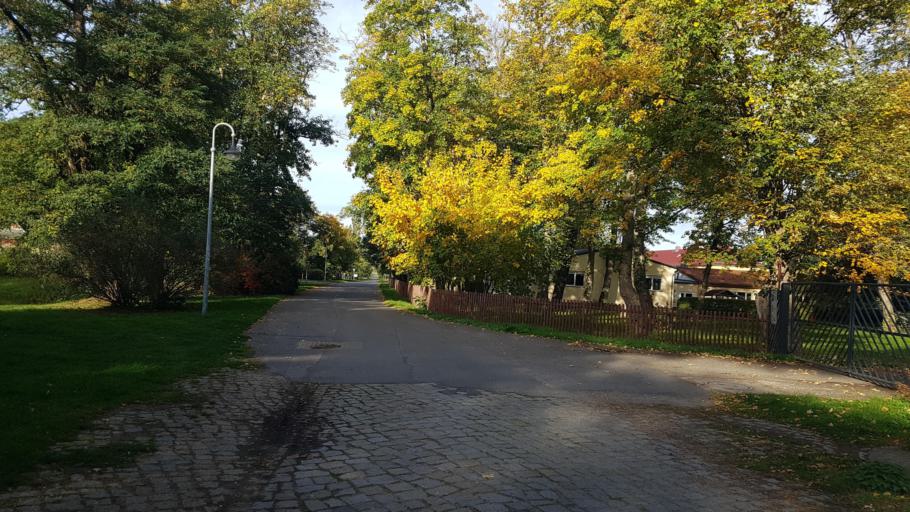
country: DE
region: Brandenburg
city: Drahnsdorf
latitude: 51.8482
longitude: 13.5260
